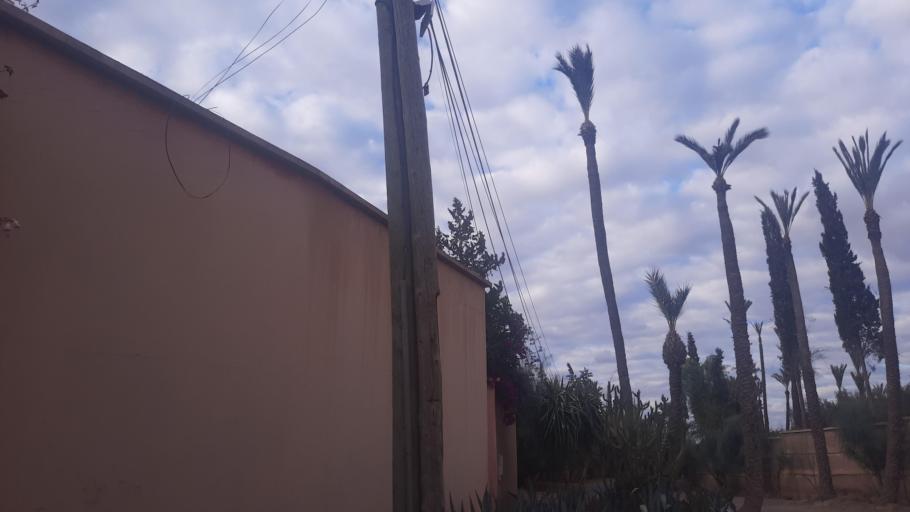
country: MA
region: Marrakech-Tensift-Al Haouz
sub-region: Marrakech
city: Marrakesh
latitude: 31.6748
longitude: -7.9531
